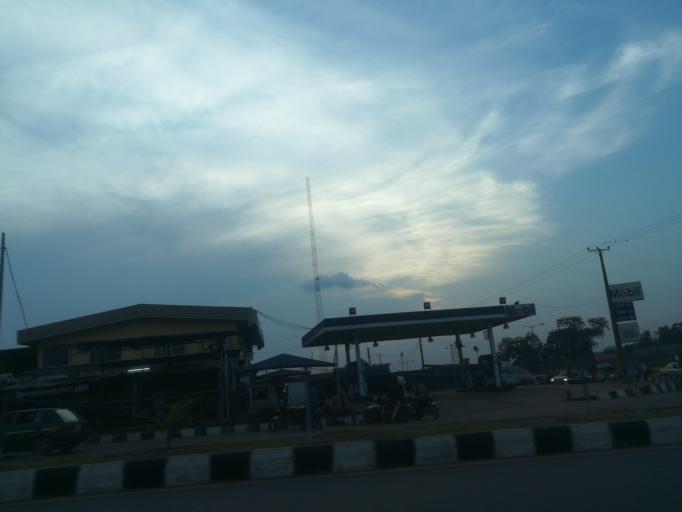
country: NG
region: Ogun
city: Abeokuta
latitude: 7.1718
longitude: 3.3709
